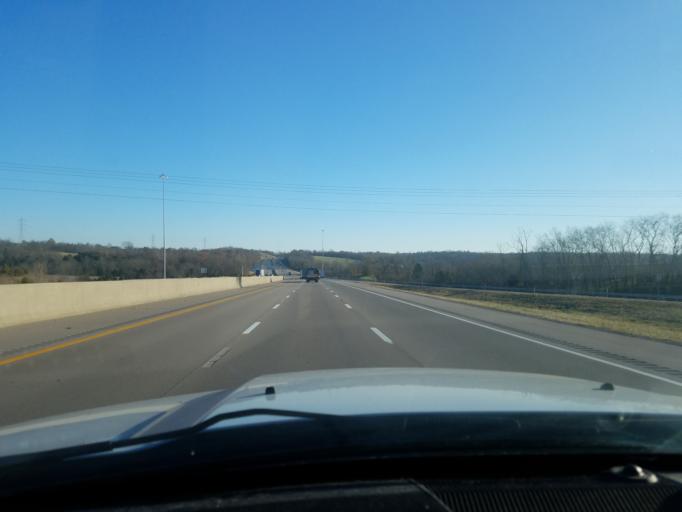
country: US
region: Kentucky
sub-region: Gallatin County
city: Warsaw
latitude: 38.7038
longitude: -84.9082
